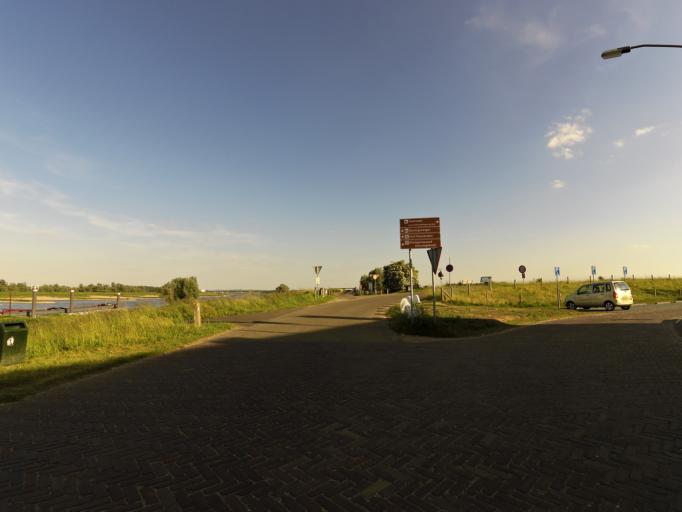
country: NL
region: Gelderland
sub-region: Gemeente Duiven
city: Duiven
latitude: 51.8893
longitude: 6.0231
